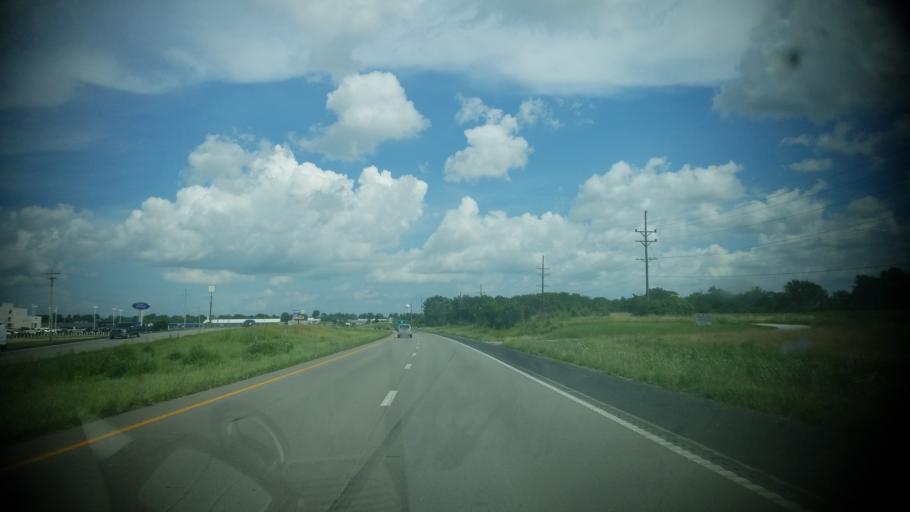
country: US
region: Missouri
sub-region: Lincoln County
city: Moscow Mills
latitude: 38.9537
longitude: -90.9382
